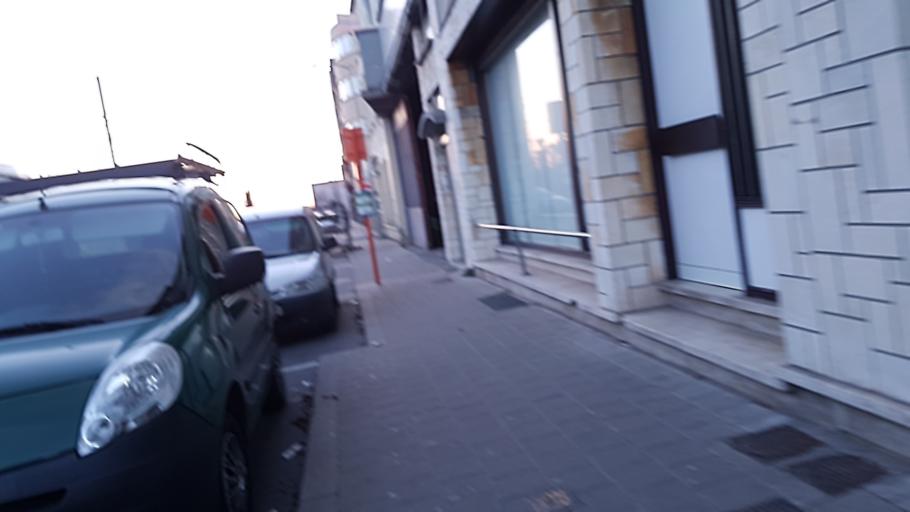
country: BE
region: Flanders
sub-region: Provincie West-Vlaanderen
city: Kortrijk
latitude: 50.8250
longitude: 3.2717
